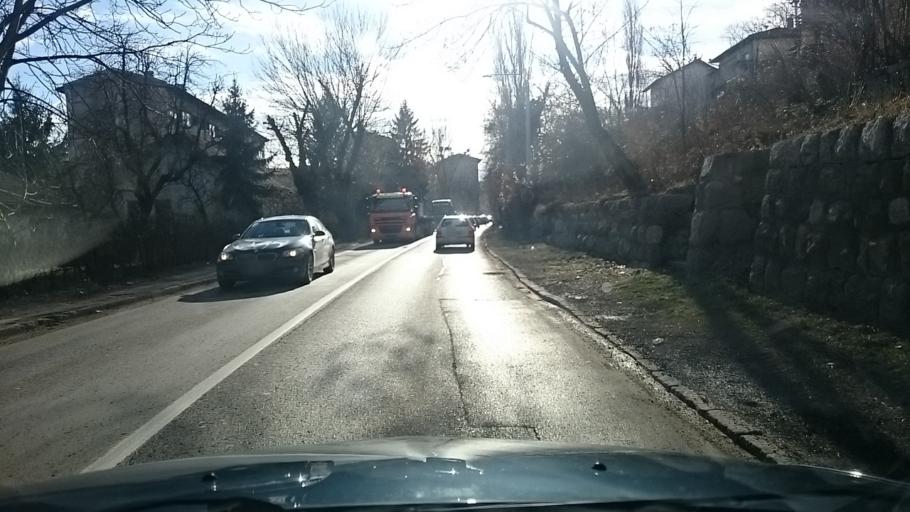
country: BA
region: Republika Srpska
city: Hiseti
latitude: 44.7684
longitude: 17.1809
